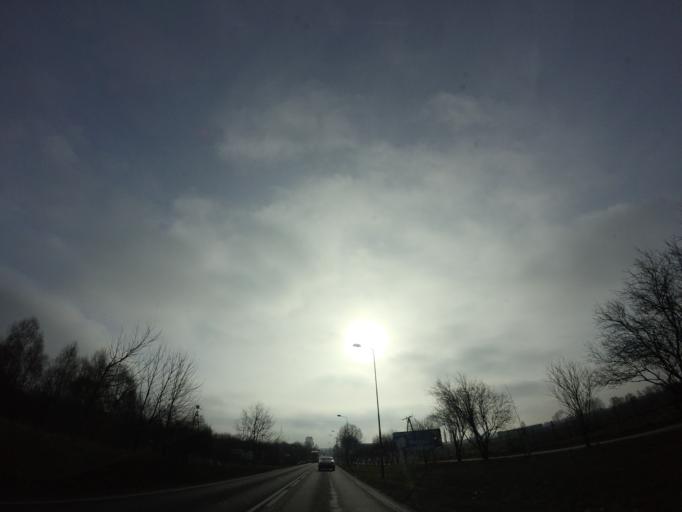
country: PL
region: West Pomeranian Voivodeship
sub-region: Powiat walecki
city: Walcz
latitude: 53.2853
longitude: 16.4450
